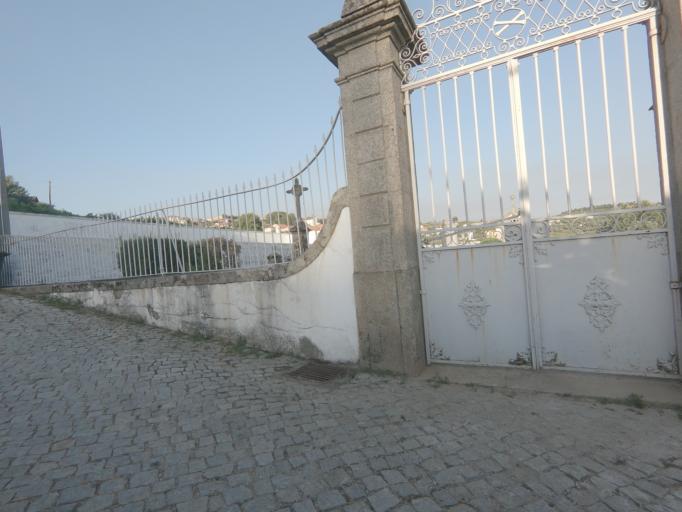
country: PT
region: Viseu
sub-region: Armamar
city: Armamar
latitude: 41.1838
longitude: -7.6884
